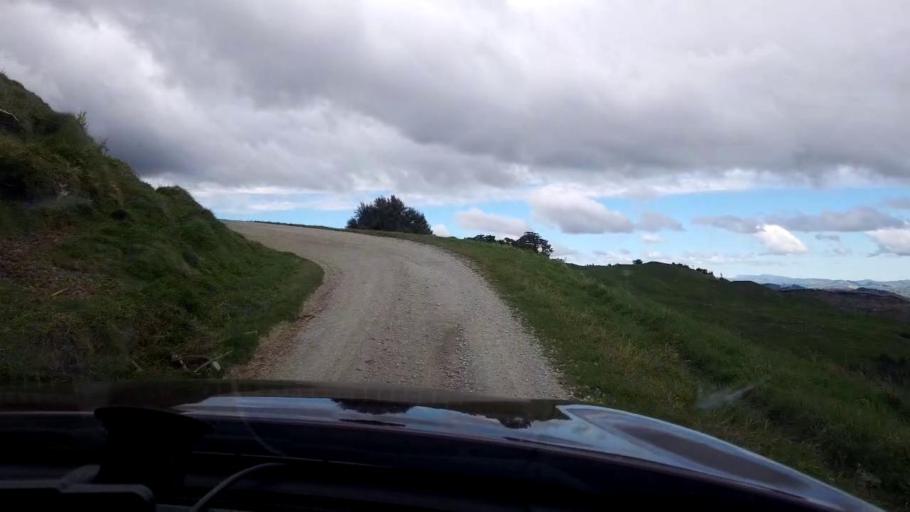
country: NZ
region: Gisborne
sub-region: Gisborne District
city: Gisborne
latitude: -38.3715
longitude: 177.9671
